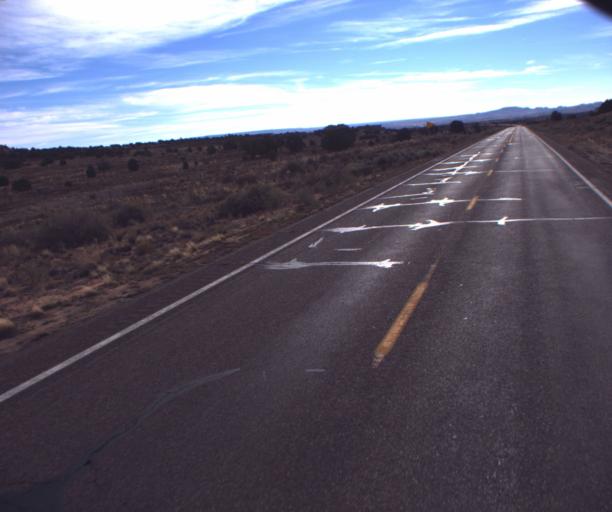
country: US
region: Arizona
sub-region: Coconino County
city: Kaibito
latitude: 36.6647
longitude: -111.2510
